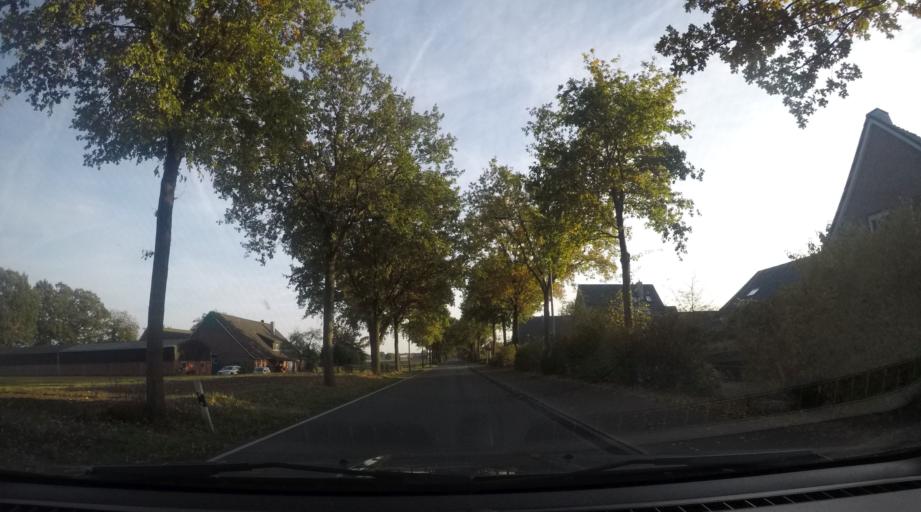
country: DE
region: North Rhine-Westphalia
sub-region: Regierungsbezirk Dusseldorf
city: Bocholt
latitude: 51.8214
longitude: 6.6325
